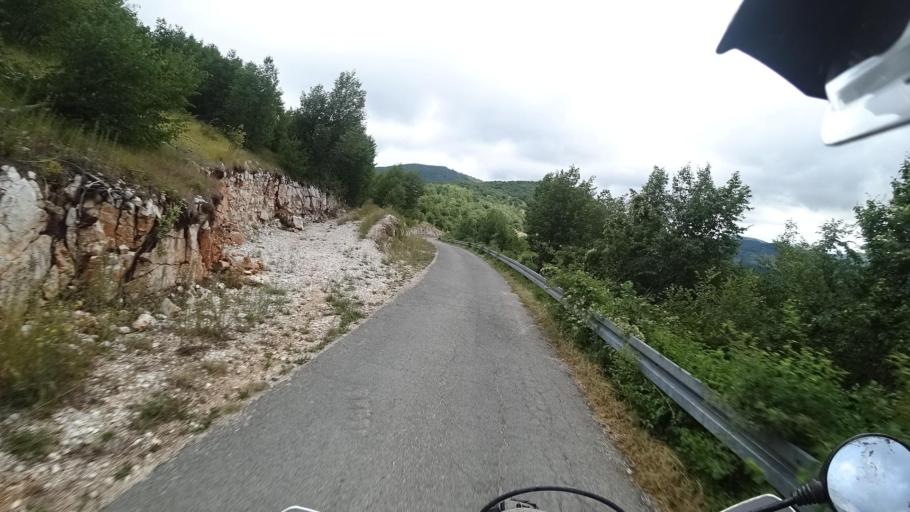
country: HR
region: Licko-Senjska
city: Jezerce
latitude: 44.7500
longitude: 15.4879
